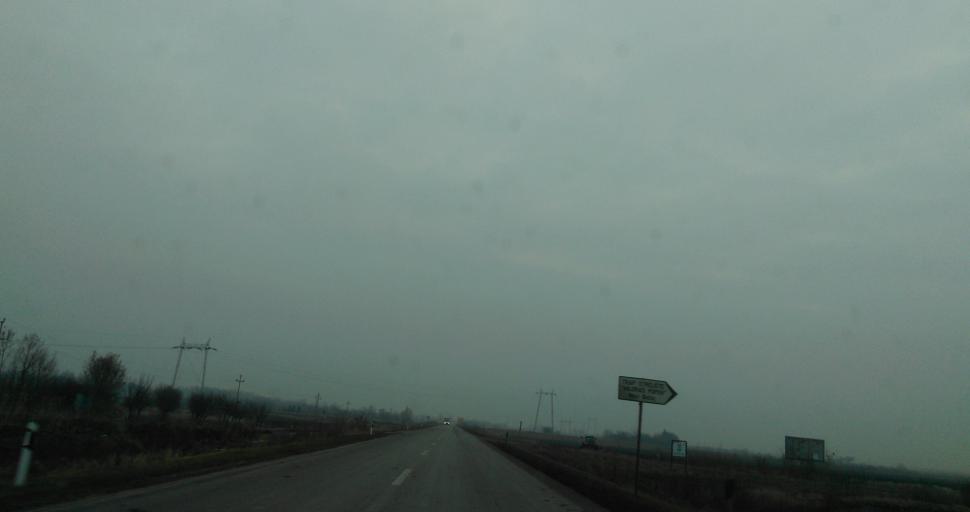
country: RS
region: Autonomna Pokrajina Vojvodina
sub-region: Srednjebanatski Okrug
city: Novi Becej
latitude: 45.5751
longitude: 20.1331
